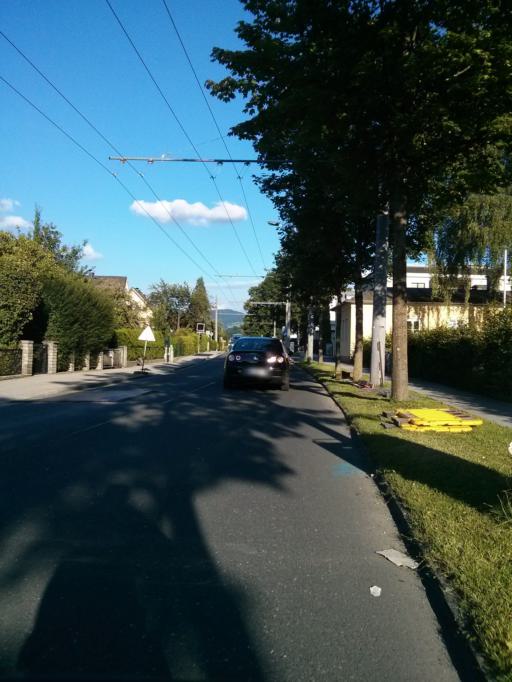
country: AT
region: Salzburg
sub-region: Politischer Bezirk Salzburg-Umgebung
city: Bergheim
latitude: 47.8106
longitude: 13.0078
